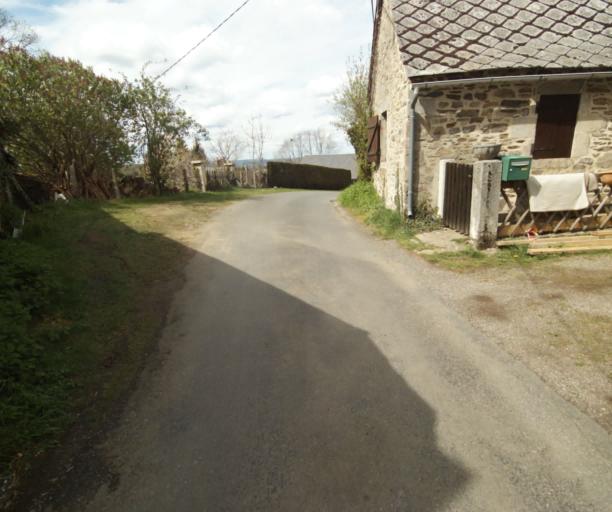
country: FR
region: Limousin
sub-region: Departement de la Correze
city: Laguenne
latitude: 45.2198
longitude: 1.8664
